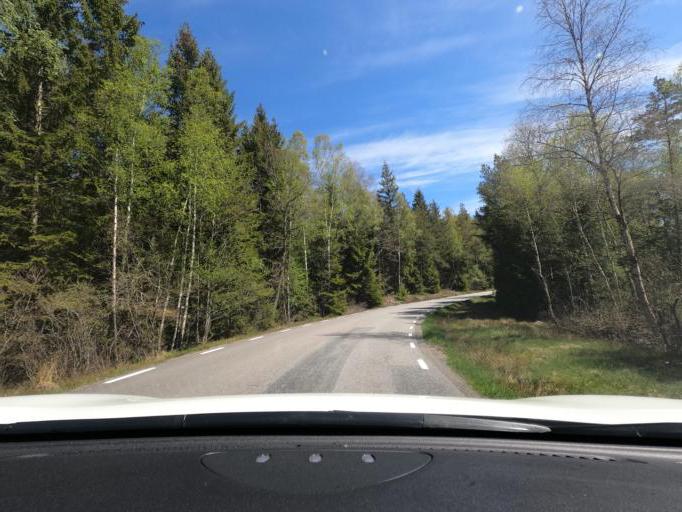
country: SE
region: Vaestra Goetaland
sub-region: Marks Kommun
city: Horred
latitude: 57.4247
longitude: 12.3768
